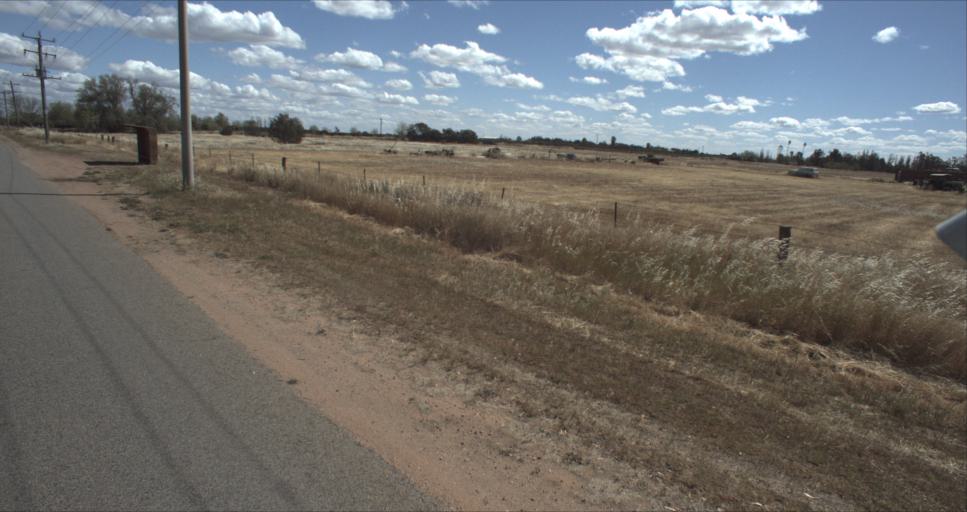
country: AU
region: New South Wales
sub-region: Leeton
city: Leeton
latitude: -34.5137
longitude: 146.2516
